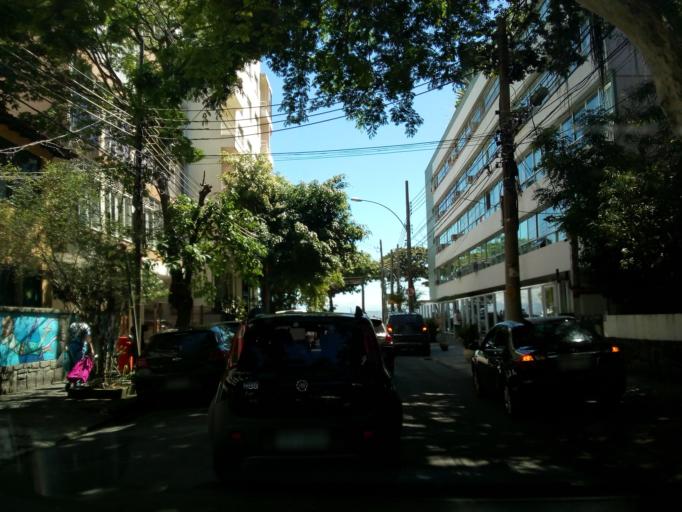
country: BR
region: Rio de Janeiro
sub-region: Rio De Janeiro
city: Rio de Janeiro
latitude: -22.9441
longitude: -43.1604
